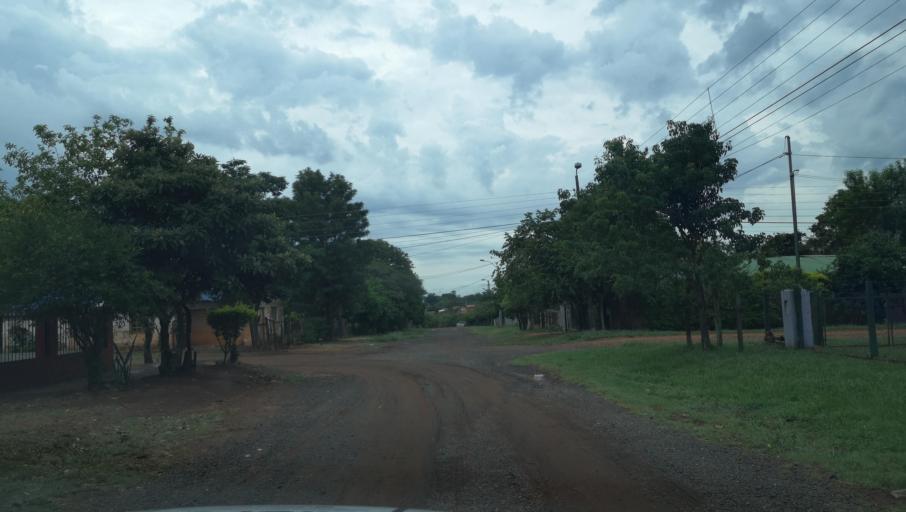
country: PY
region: Misiones
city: Santa Maria
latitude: -26.8901
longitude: -57.0412
